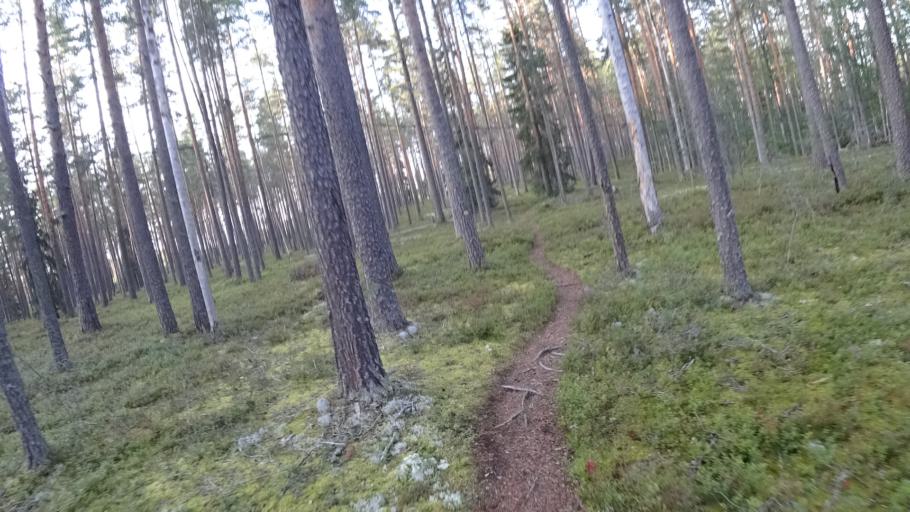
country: FI
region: North Karelia
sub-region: Joensuu
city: Ilomantsi
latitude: 62.5833
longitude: 31.1848
